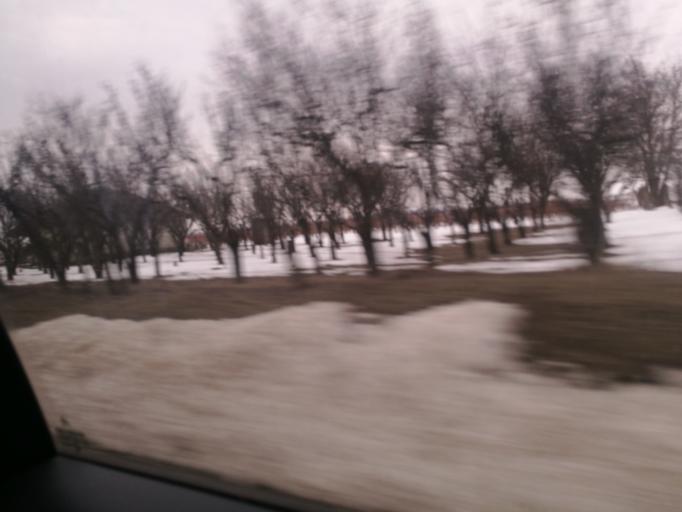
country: RO
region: Iasi
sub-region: Comuna Costesti
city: Costesti
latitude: 47.2424
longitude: 26.8998
